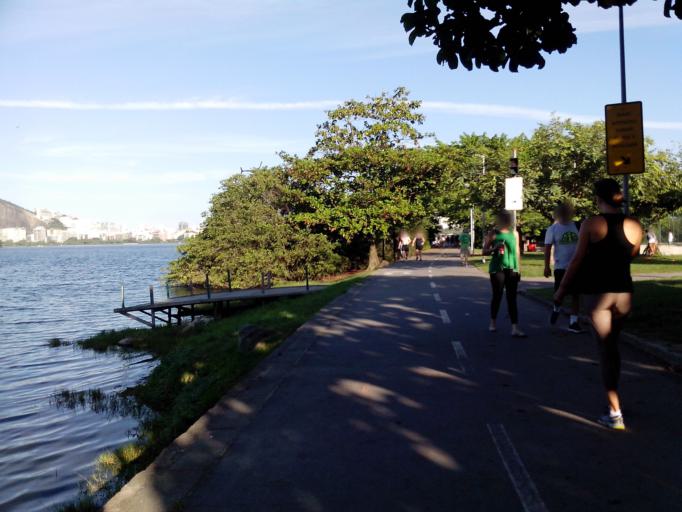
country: BR
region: Rio de Janeiro
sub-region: Rio De Janeiro
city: Rio de Janeiro
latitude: -22.9695
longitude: -43.2166
